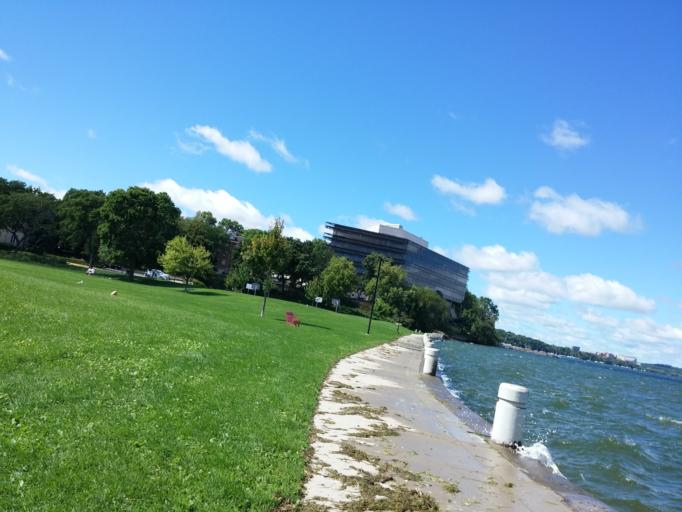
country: US
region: Wisconsin
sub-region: Dane County
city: Madison
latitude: 43.0813
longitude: -89.3839
